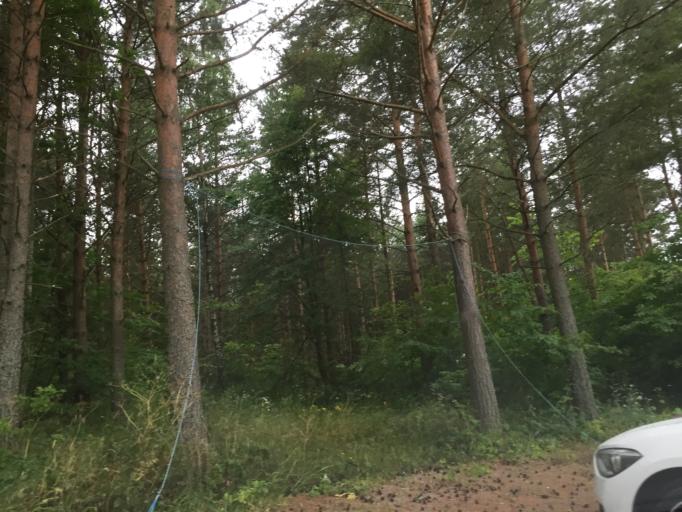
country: SE
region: OEstergoetland
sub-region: Vadstena Kommun
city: Vadstena
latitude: 58.4730
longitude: 14.8403
